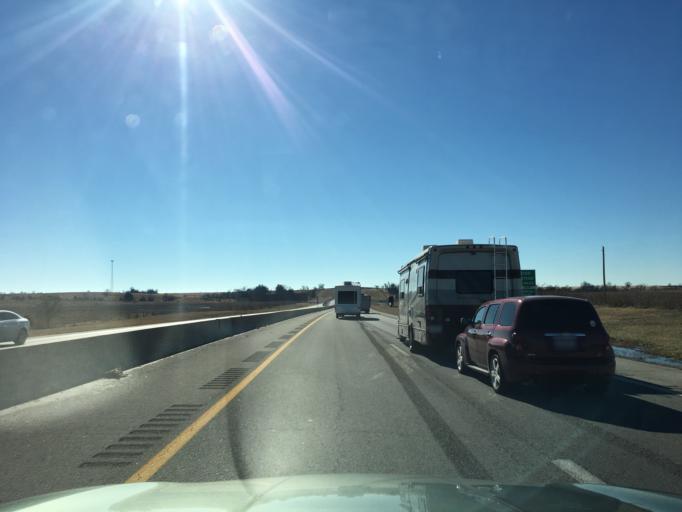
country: US
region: Oklahoma
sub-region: Kay County
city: Blackwell
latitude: 37.0115
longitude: -97.3389
